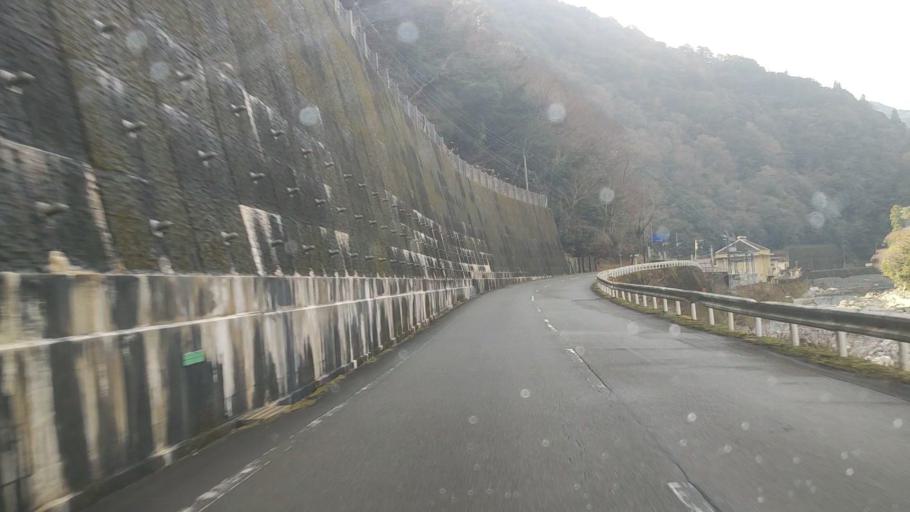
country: JP
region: Kumamoto
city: Hitoyoshi
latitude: 32.4213
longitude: 130.8554
